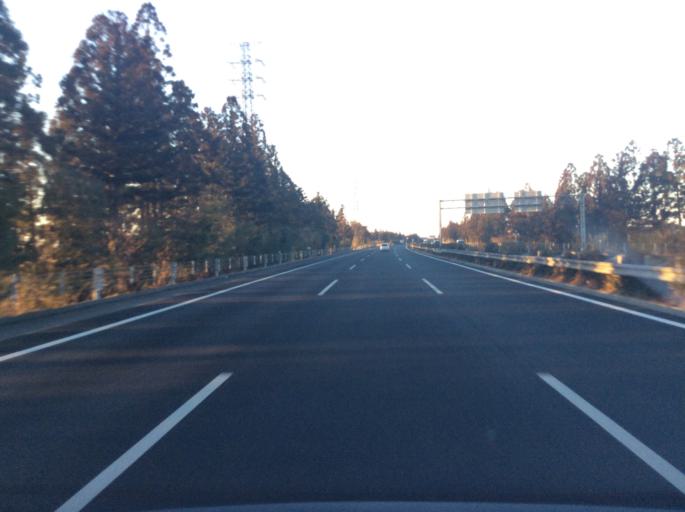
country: JP
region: Ibaraki
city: Mito-shi
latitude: 36.3690
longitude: 140.3823
